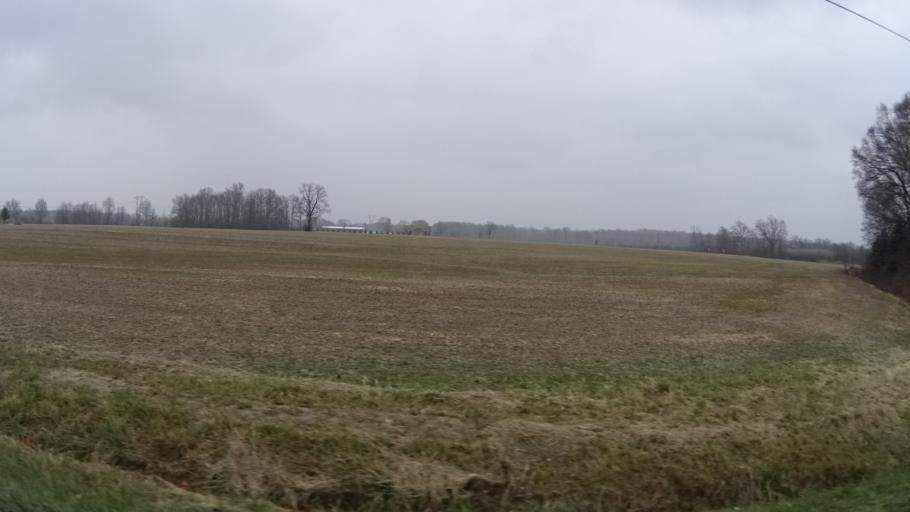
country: US
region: Ohio
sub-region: Lorain County
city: Oberlin
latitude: 41.3100
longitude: -82.1966
